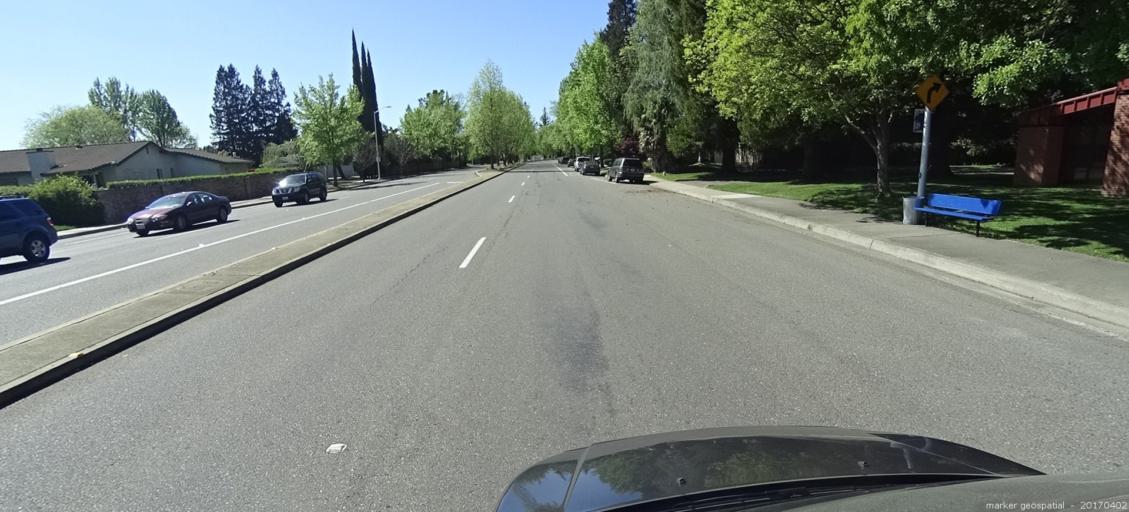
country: US
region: California
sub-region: Sacramento County
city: Parkway
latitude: 38.4975
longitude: -121.5312
